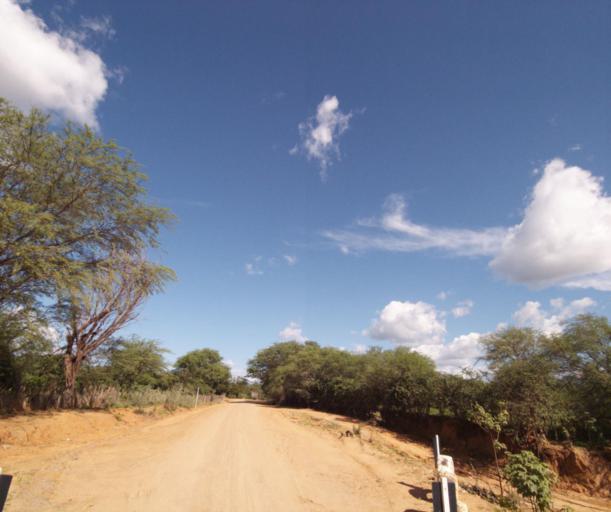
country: BR
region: Bahia
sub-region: Pocoes
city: Pocoes
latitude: -14.2415
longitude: -40.7774
